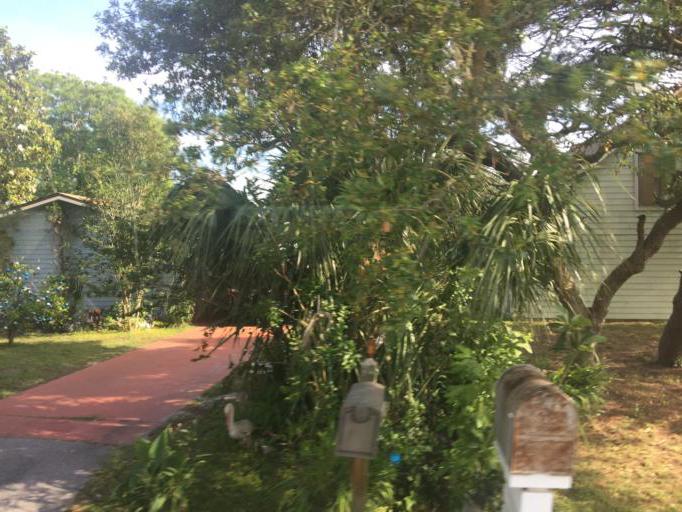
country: US
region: Florida
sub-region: Bay County
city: Laguna Beach
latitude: 30.2543
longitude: -85.9523
